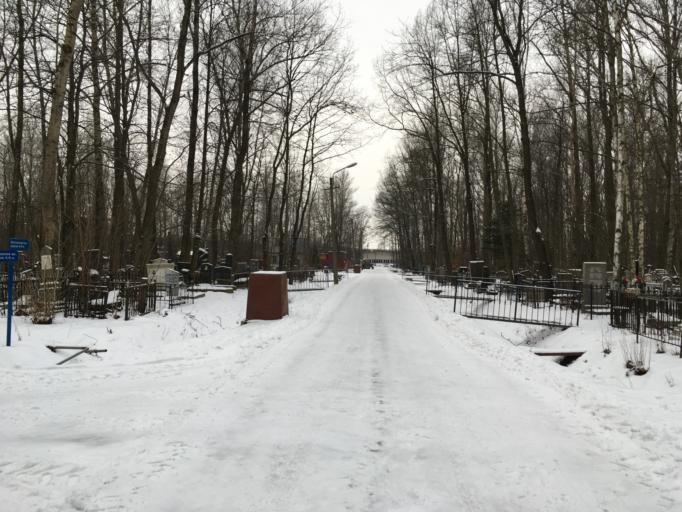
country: RU
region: St.-Petersburg
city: Obukhovo
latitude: 59.8558
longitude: 30.4522
